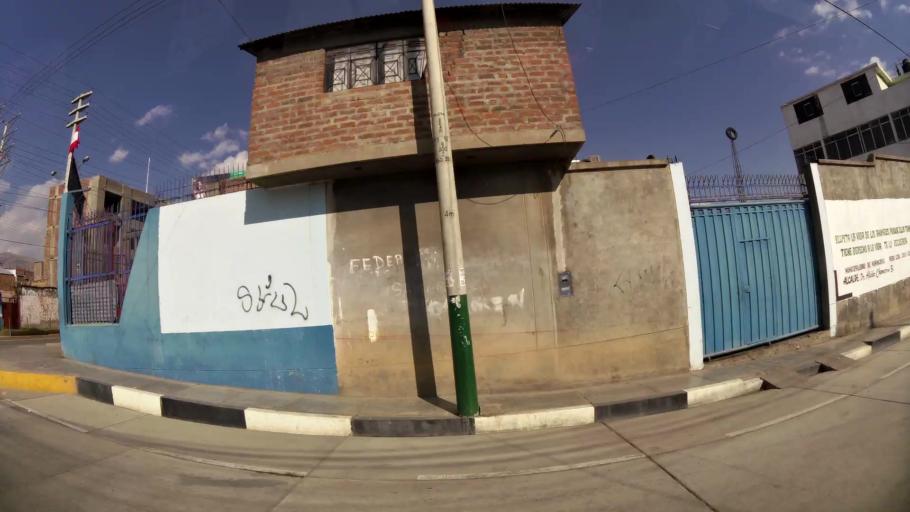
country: PE
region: Junin
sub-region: Provincia de Huancayo
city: El Tambo
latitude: -12.0616
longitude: -75.2202
